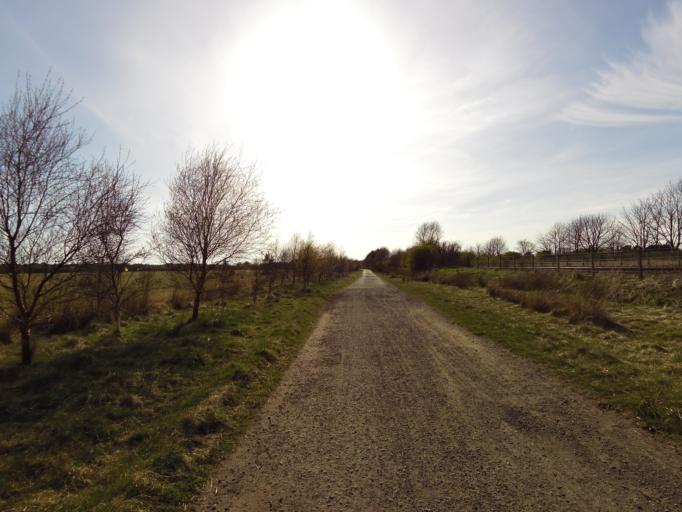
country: GB
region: Scotland
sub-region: Angus
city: Carnoustie
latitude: 56.4940
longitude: -2.7404
